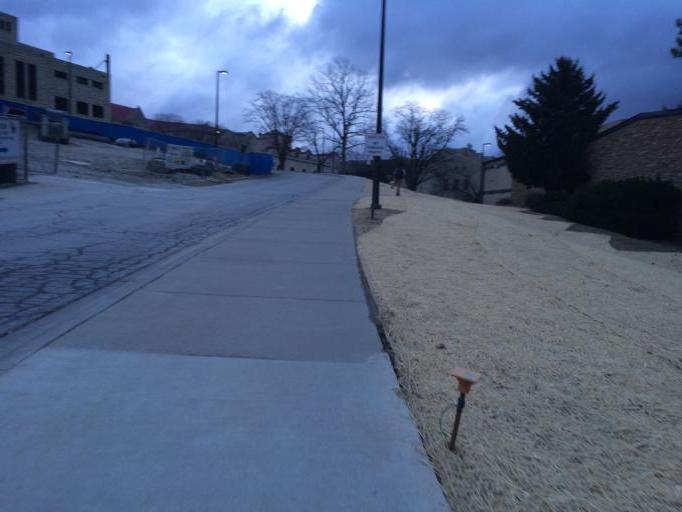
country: US
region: Kansas
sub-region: Douglas County
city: Lawrence
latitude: 38.9571
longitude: -95.2519
